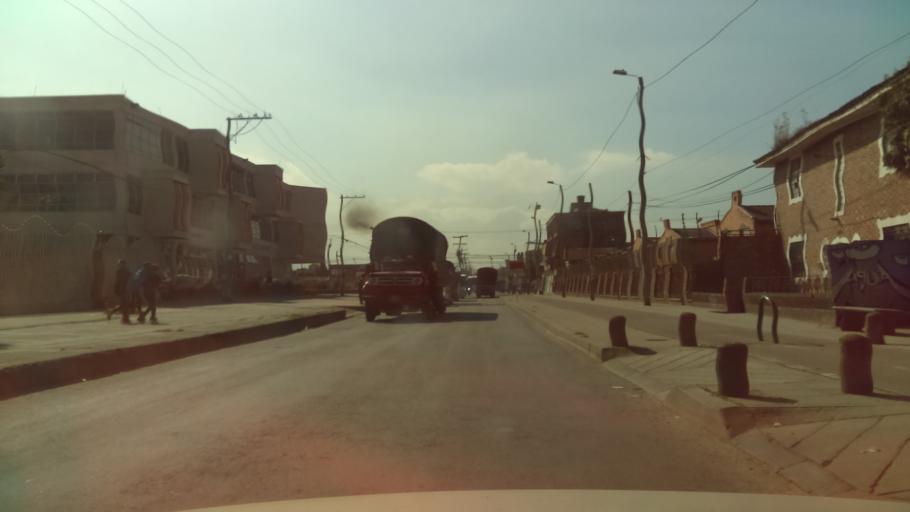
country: CO
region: Cundinamarca
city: Funza
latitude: 4.7105
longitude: -74.2075
